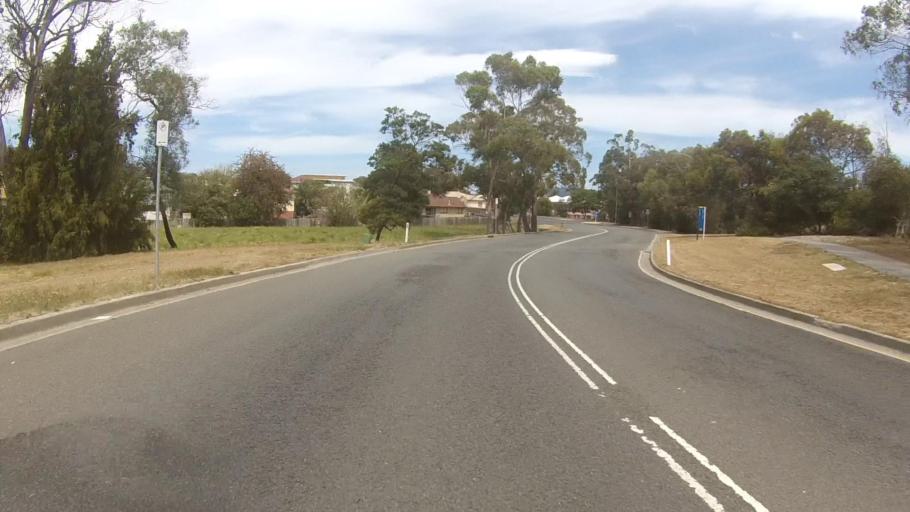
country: AU
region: Tasmania
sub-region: Clarence
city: Warrane
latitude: -42.8608
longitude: 147.3717
